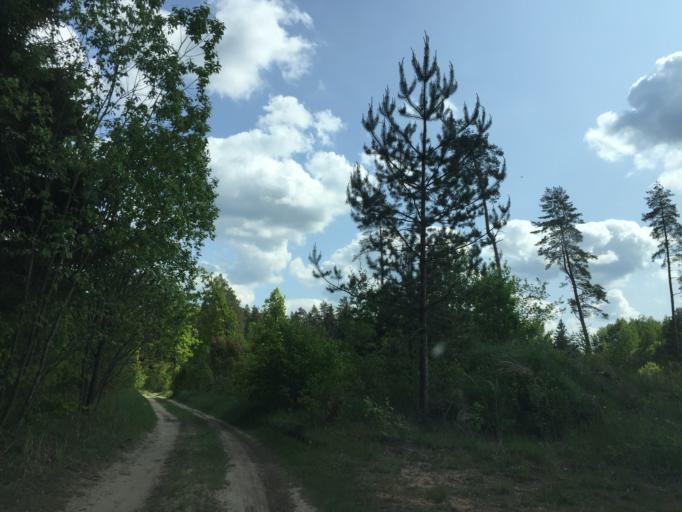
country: LV
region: Baldone
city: Baldone
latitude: 56.8043
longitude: 24.4248
